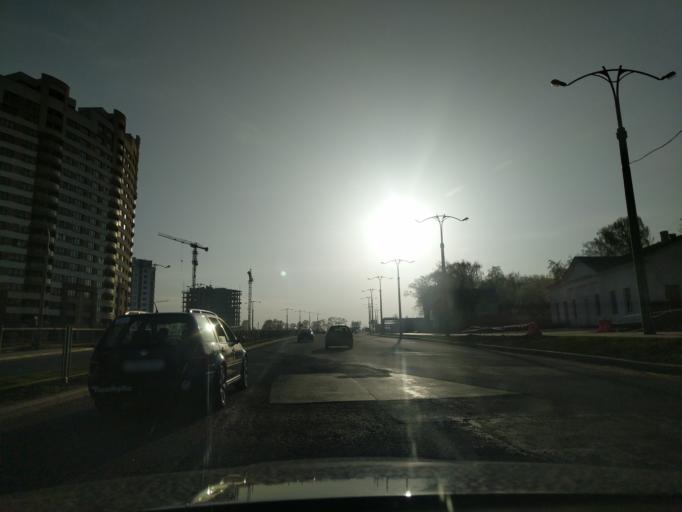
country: BY
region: Minsk
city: Minsk
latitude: 53.8720
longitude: 27.5578
